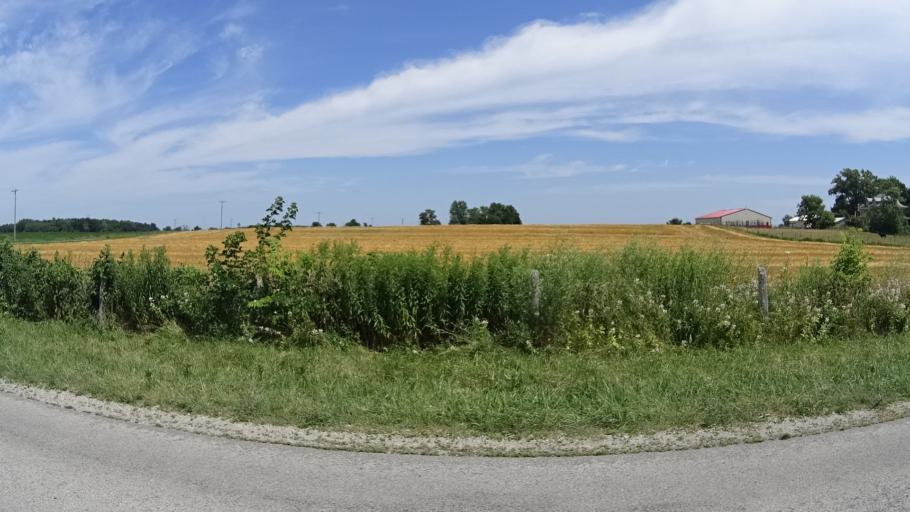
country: US
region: Ohio
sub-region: Erie County
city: Sandusky
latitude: 41.3791
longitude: -82.7871
